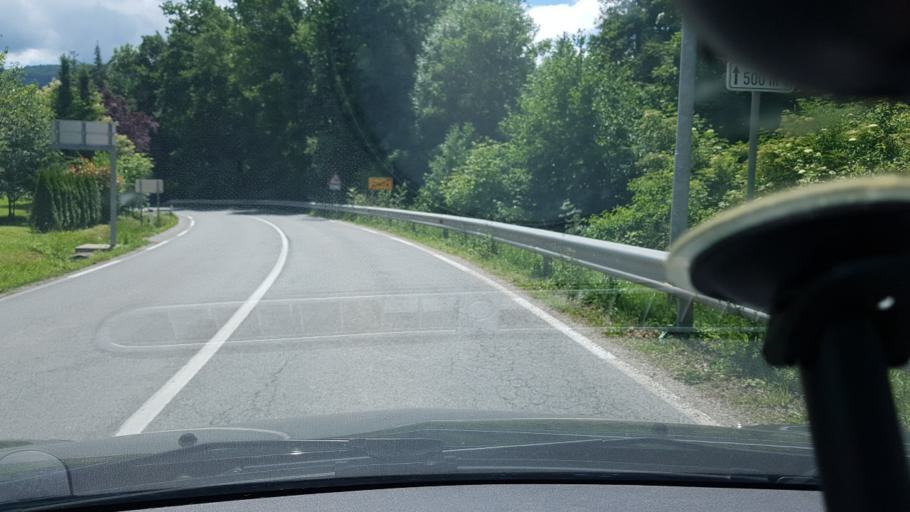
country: SI
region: Zrece
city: Zrece
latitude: 46.3643
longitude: 15.3924
